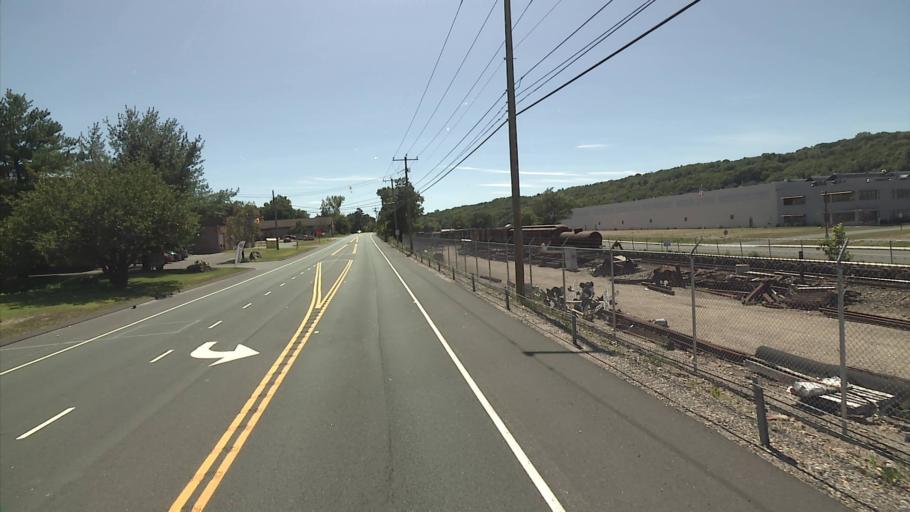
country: US
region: Connecticut
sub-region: Litchfield County
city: Oakville
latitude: 41.5978
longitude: -73.0577
